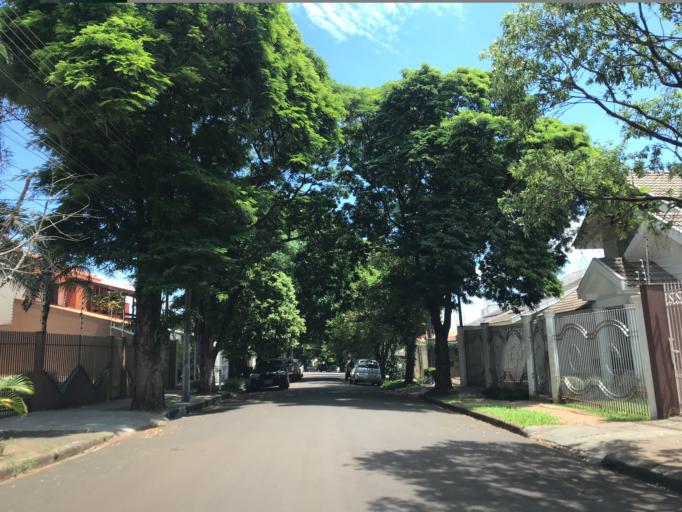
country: BR
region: Parana
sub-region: Maringa
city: Maringa
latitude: -23.4434
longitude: -51.9562
